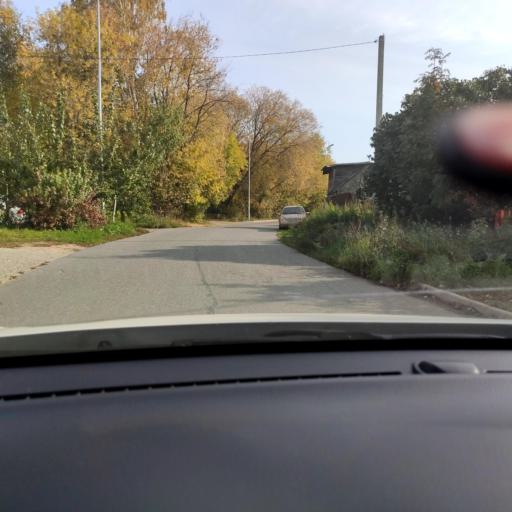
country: RU
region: Tatarstan
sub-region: Gorod Kazan'
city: Kazan
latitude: 55.7390
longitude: 49.1652
